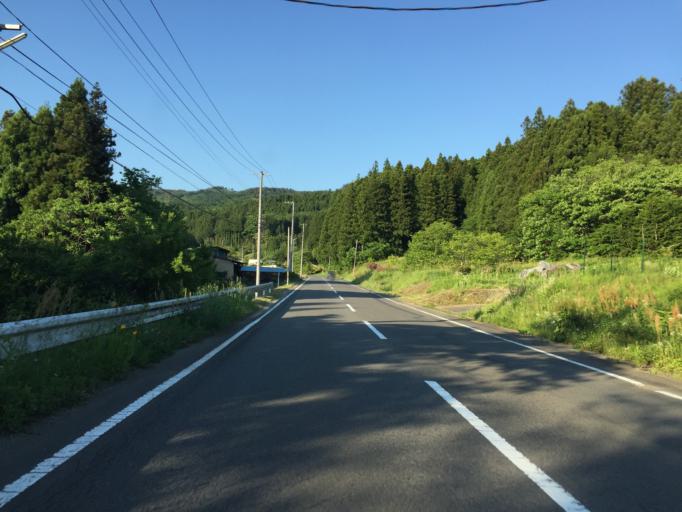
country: JP
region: Fukushima
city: Ishikawa
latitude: 36.9886
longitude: 140.4362
